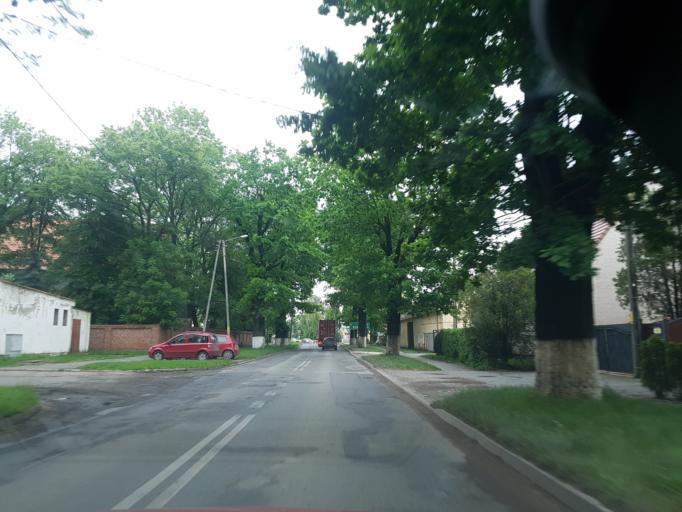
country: PL
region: Lower Silesian Voivodeship
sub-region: Powiat wroclawski
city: Zorawina
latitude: 50.9278
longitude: 17.0394
